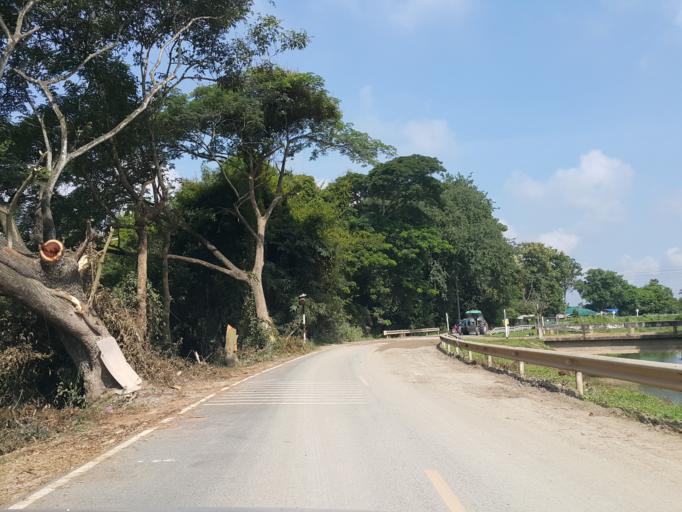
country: TH
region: Chiang Mai
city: San Sai
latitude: 18.9287
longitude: 98.9972
